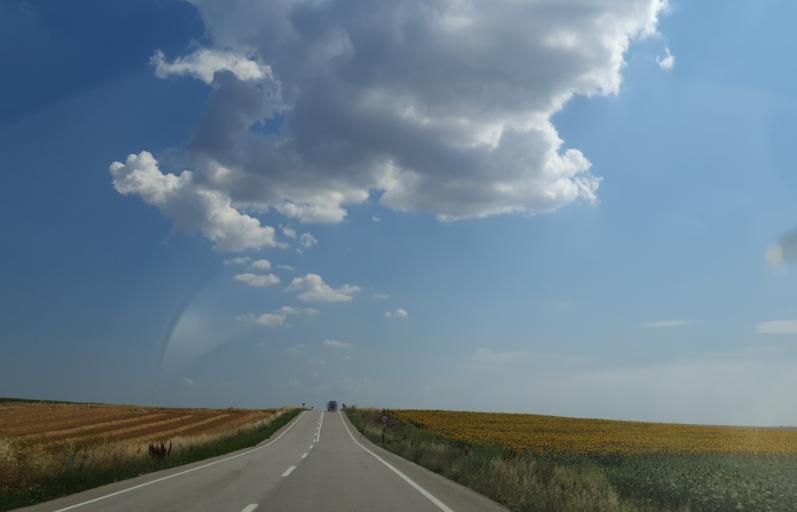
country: TR
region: Kirklareli
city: Buyukkaristiran
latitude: 41.4128
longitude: 27.5776
